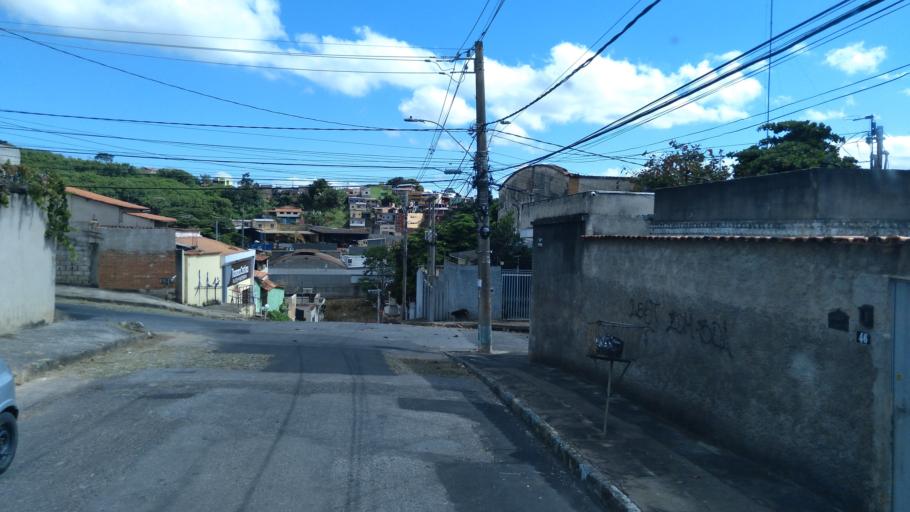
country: BR
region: Minas Gerais
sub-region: Belo Horizonte
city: Belo Horizonte
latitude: -19.8600
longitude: -43.9070
